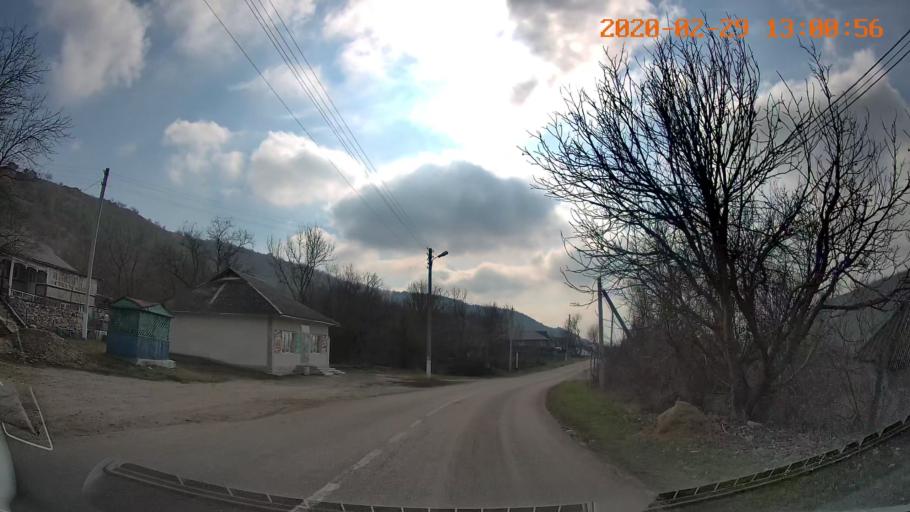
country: MD
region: Telenesti
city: Camenca
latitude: 48.0482
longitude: 28.7213
